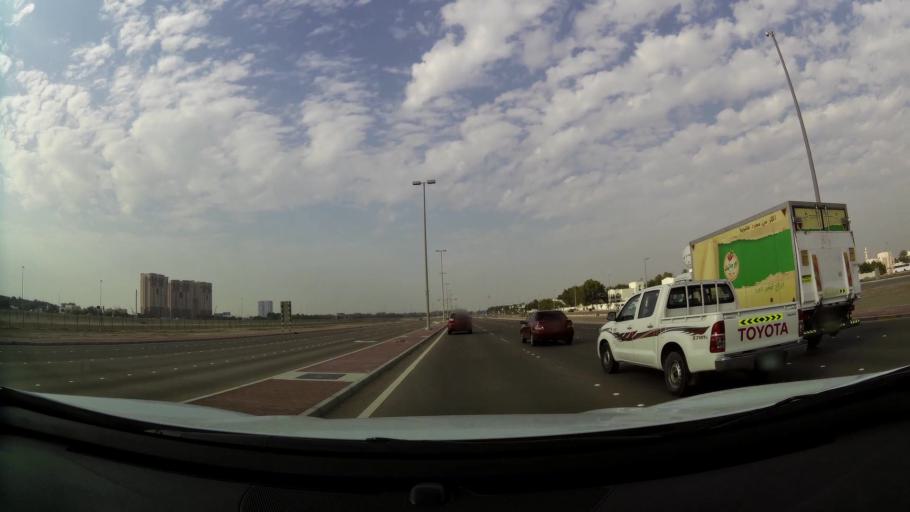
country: AE
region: Abu Dhabi
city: Abu Dhabi
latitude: 24.3789
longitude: 54.5275
